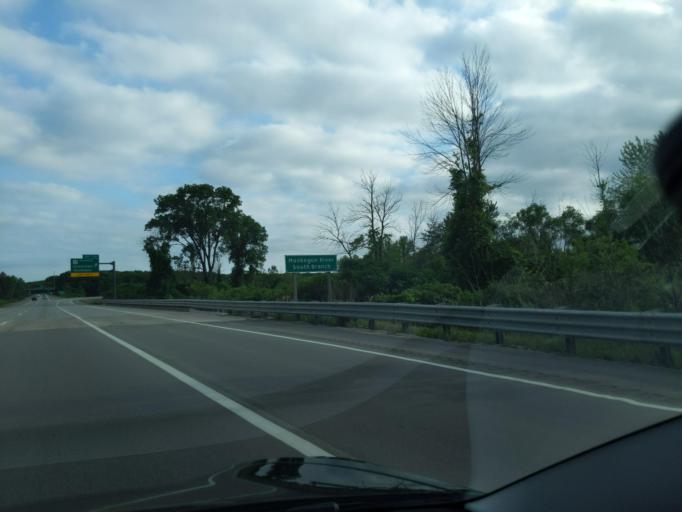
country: US
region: Michigan
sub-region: Muskegon County
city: Muskegon
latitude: 43.2634
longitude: -86.2056
